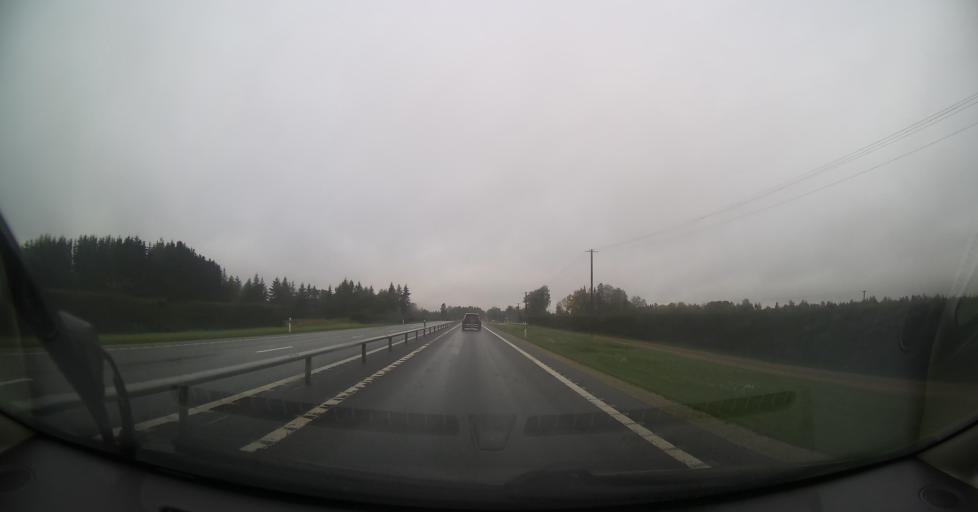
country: EE
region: Jogevamaa
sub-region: Jogeva linn
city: Jogeva
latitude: 58.5979
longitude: 26.2251
